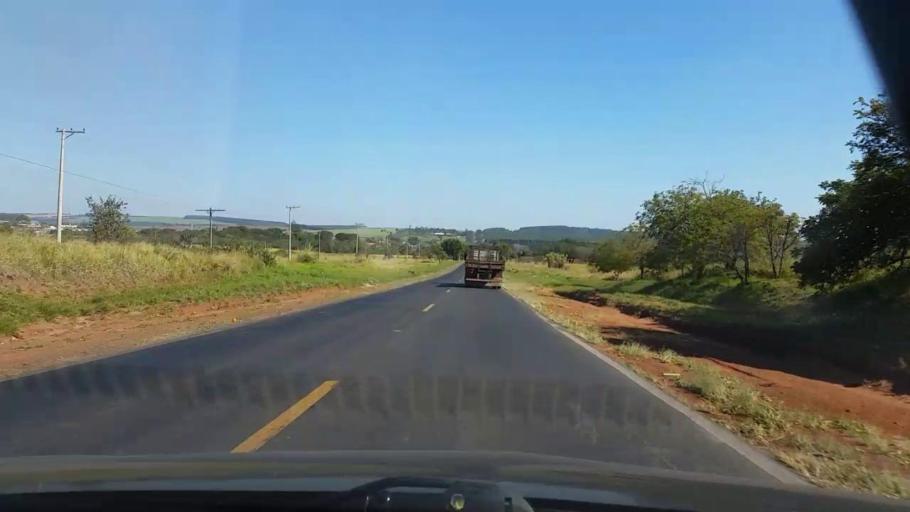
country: BR
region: Sao Paulo
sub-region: Sao Manuel
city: Sao Manuel
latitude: -22.7969
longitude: -48.6609
